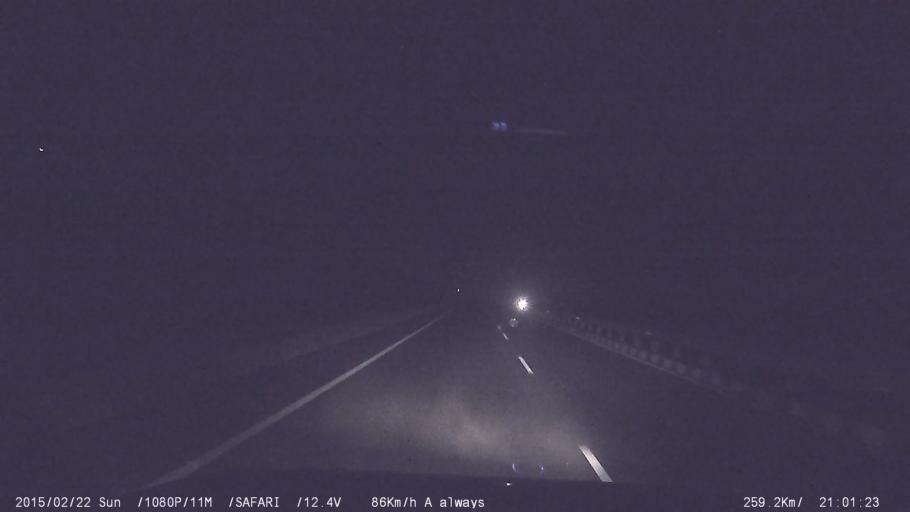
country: IN
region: Tamil Nadu
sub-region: Karur
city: Pallappatti
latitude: 10.6639
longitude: 77.9345
